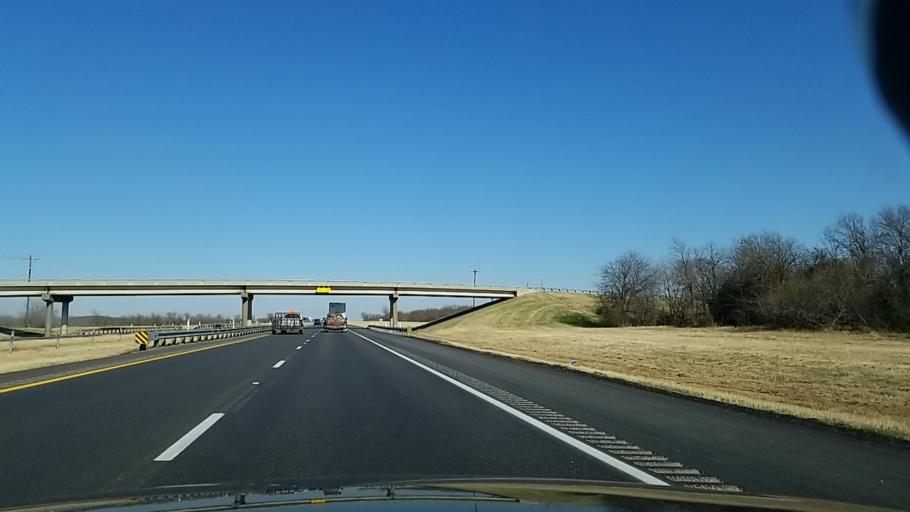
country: US
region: Texas
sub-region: Denton County
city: Argyle
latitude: 33.1173
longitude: -97.2151
